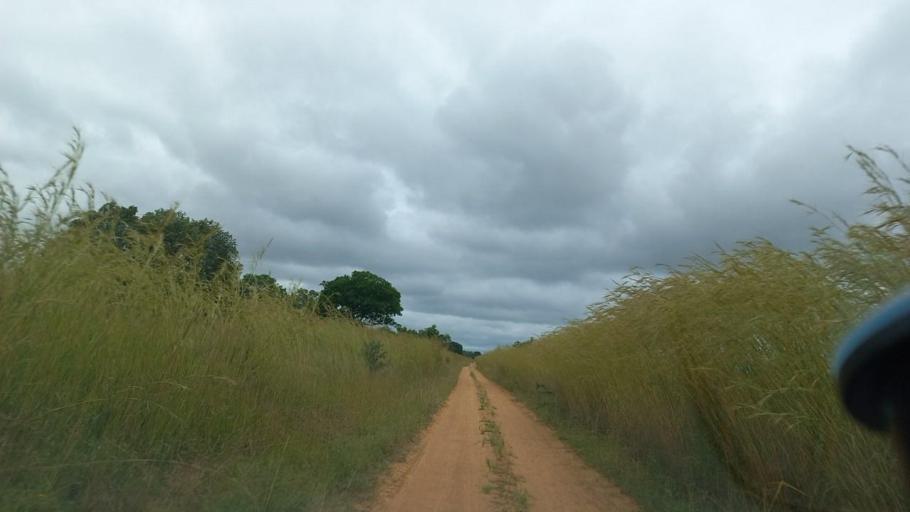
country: ZM
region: Lusaka
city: Lusaka
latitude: -15.1306
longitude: 28.3695
